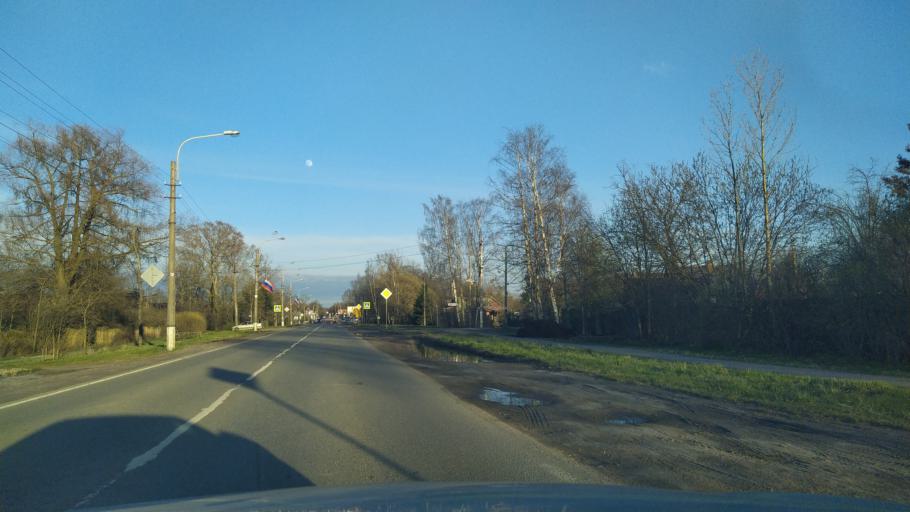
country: RU
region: St.-Petersburg
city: Aleksandrovskaya
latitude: 59.7352
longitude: 30.3358
